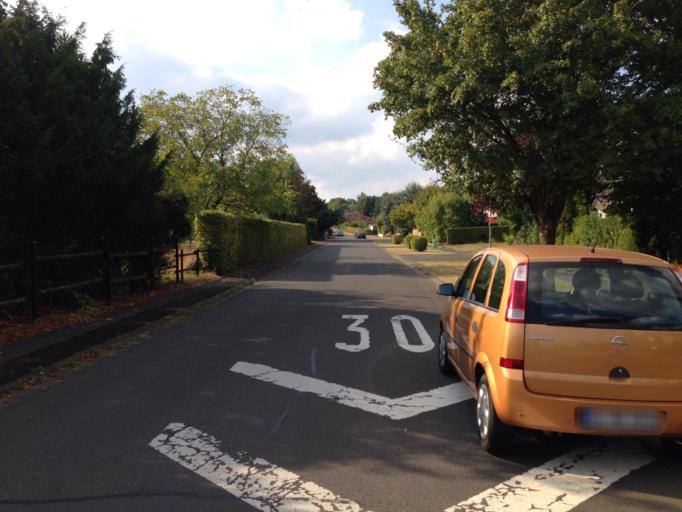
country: DE
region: Hesse
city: Lollar
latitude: 50.6403
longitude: 8.6619
